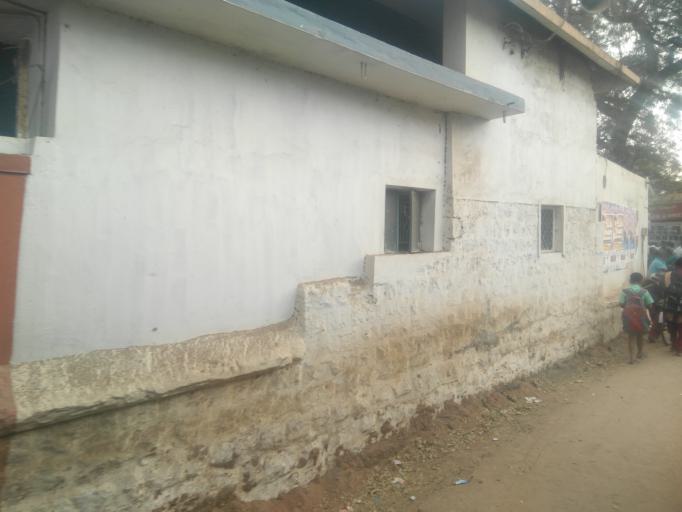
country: IN
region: Tamil Nadu
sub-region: Coimbatore
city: Coimbatore
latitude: 11.0648
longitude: 76.9082
